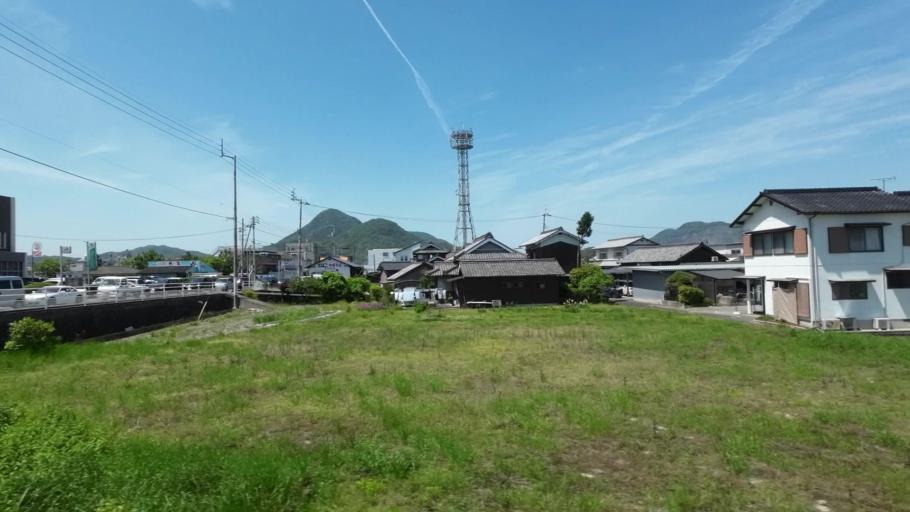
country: JP
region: Kagawa
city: Marugame
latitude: 34.2359
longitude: 133.7859
